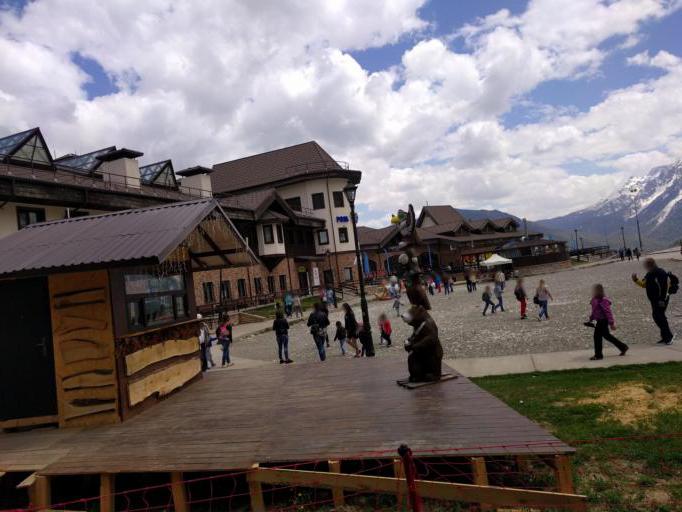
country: RU
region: Krasnodarskiy
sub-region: Sochi City
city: Krasnaya Polyana
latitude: 43.6581
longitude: 40.3193
